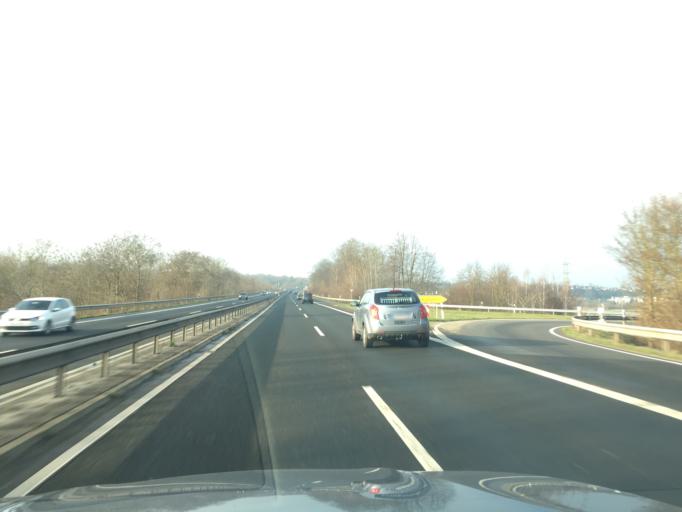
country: DE
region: Rheinland-Pfalz
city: Kettig
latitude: 50.4042
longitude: 7.4743
